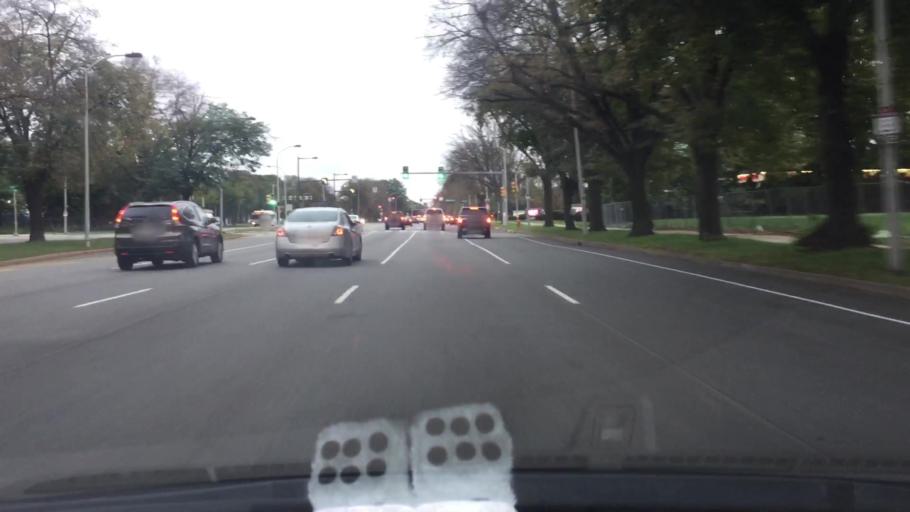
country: US
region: Pennsylvania
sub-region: Philadelphia County
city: Philadelphia
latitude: 39.9101
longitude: -75.1732
